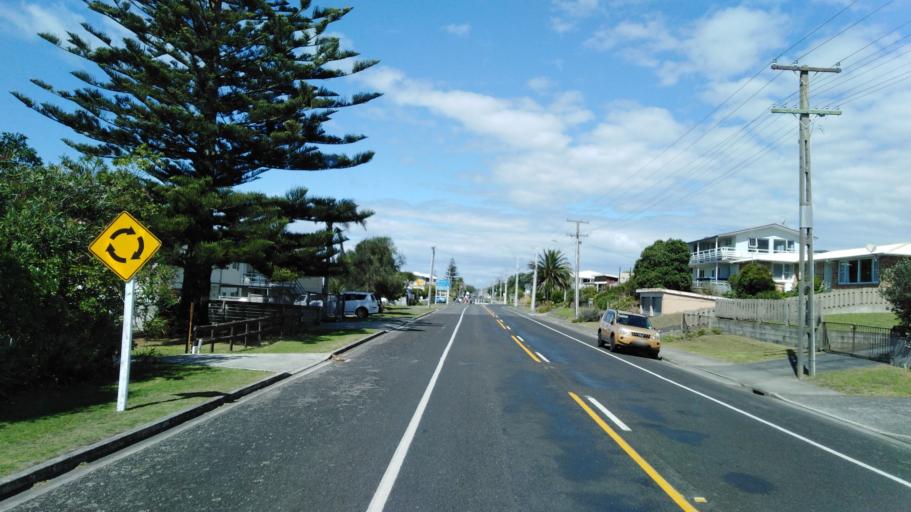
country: NZ
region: Bay of Plenty
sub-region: Western Bay of Plenty District
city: Waihi Beach
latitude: -37.4283
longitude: 175.9574
